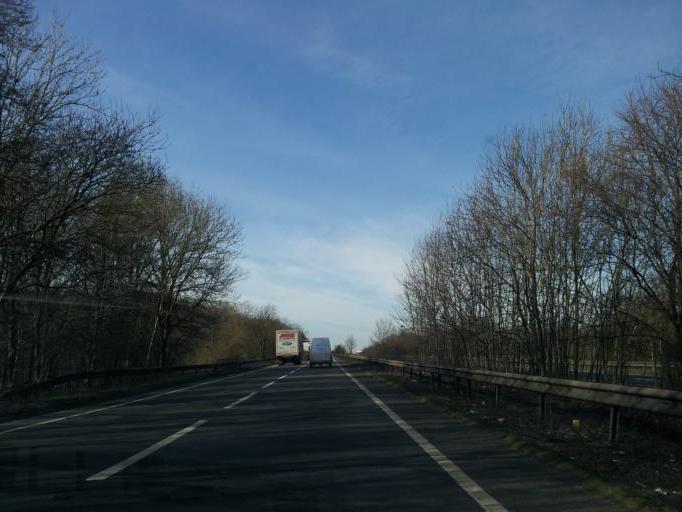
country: GB
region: England
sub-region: District of Rutland
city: Tickencote
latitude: 52.6901
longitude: -0.5600
